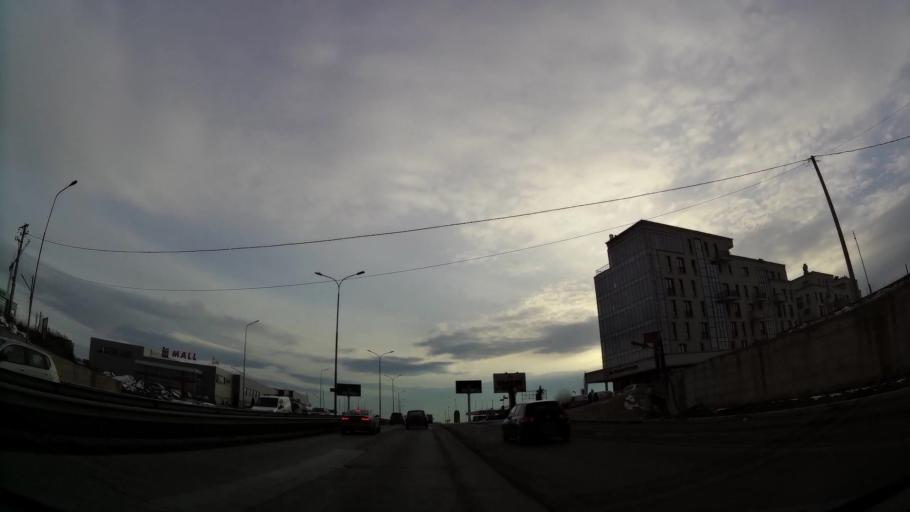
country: XK
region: Pristina
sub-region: Komuna e Prishtines
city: Pristina
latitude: 42.6354
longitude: 21.1522
